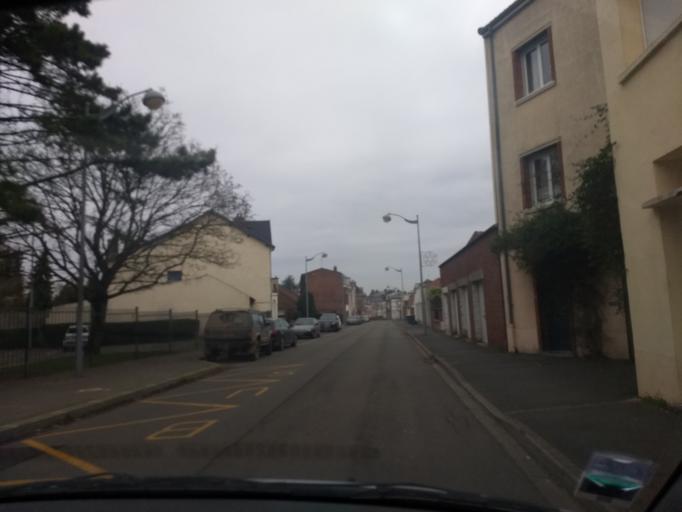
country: FR
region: Nord-Pas-de-Calais
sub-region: Departement du Pas-de-Calais
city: Arras
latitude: 50.2820
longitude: 2.7876
